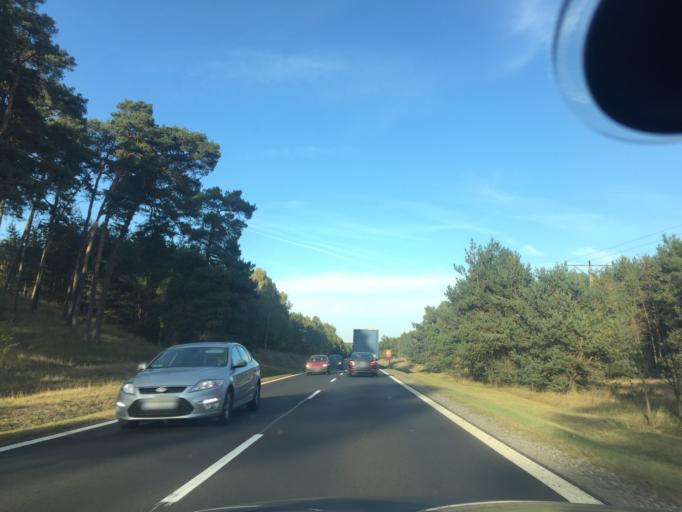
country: PL
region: Kujawsko-Pomorskie
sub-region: Powiat torunski
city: Wielka Nieszawka
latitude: 52.9295
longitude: 18.5075
